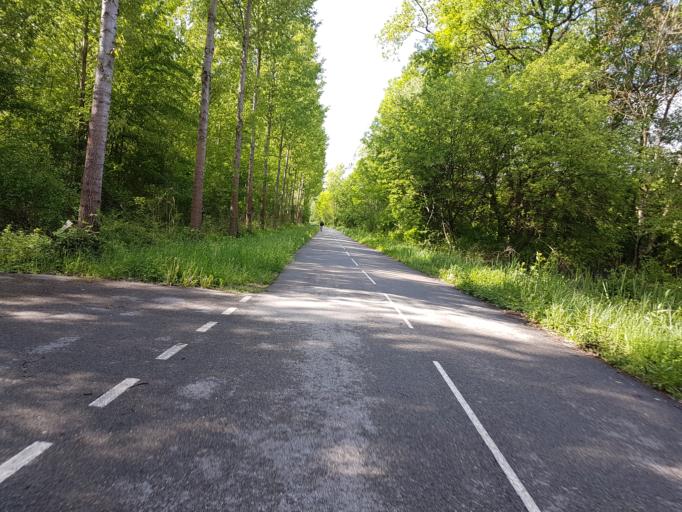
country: FR
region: Rhone-Alpes
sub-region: Departement de l'Ain
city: Culoz
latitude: 45.8600
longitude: 5.8224
